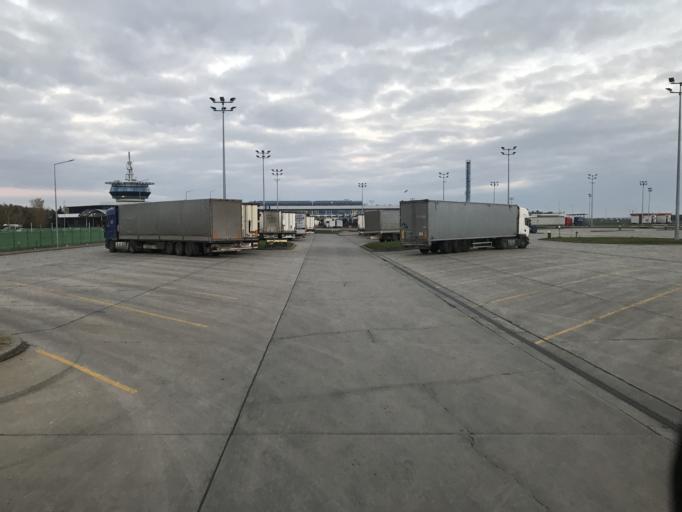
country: PL
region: Lublin Voivodeship
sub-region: Powiat bialski
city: Terespol
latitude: 52.0751
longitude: 23.5101
